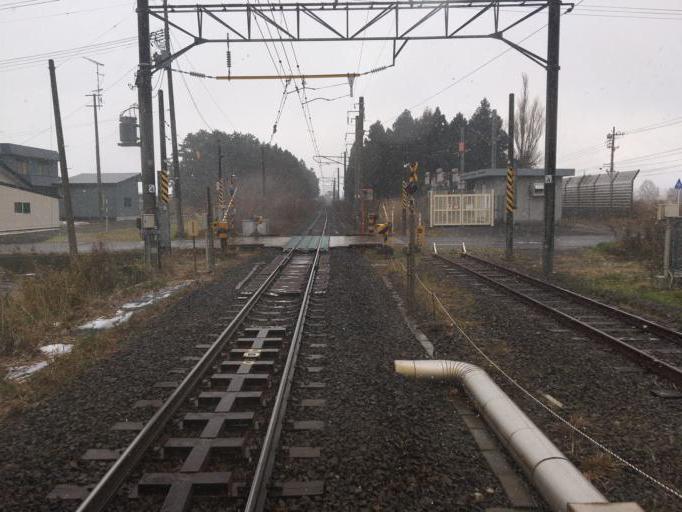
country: JP
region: Aomori
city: Aomori Shi
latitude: 40.9865
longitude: 140.6527
